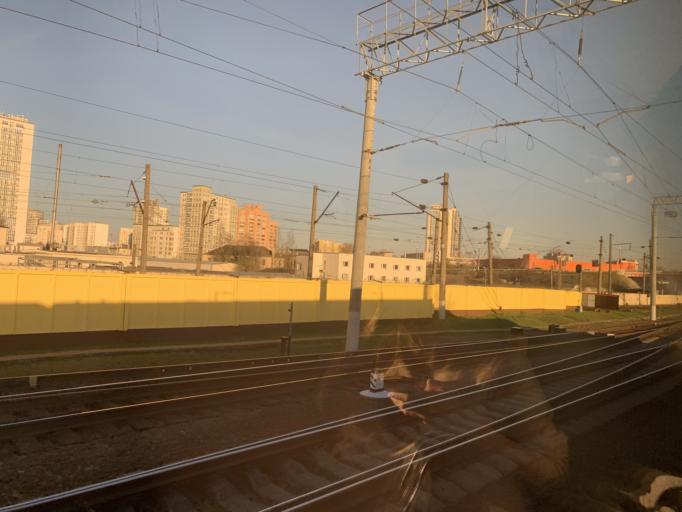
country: BY
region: Minsk
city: Minsk
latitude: 53.9116
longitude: 27.5224
